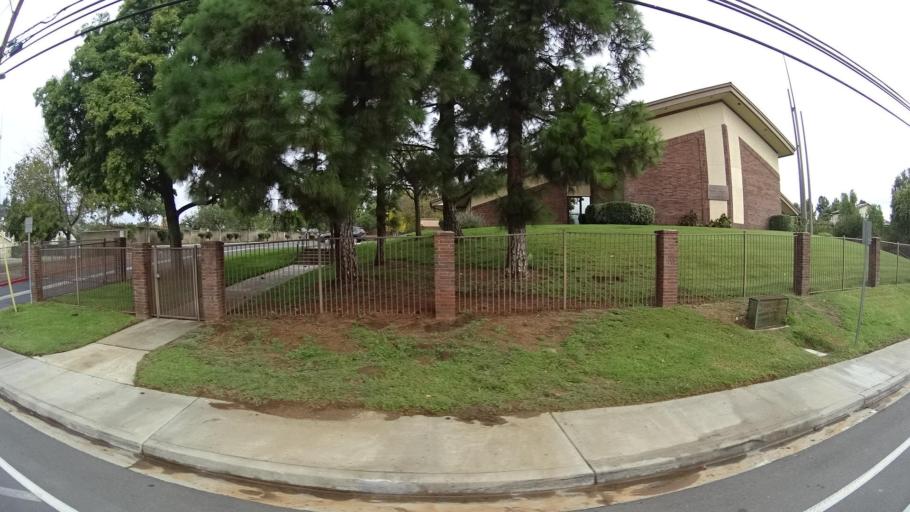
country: US
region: California
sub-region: San Diego County
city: Rancho San Diego
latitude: 32.7621
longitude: -116.9231
